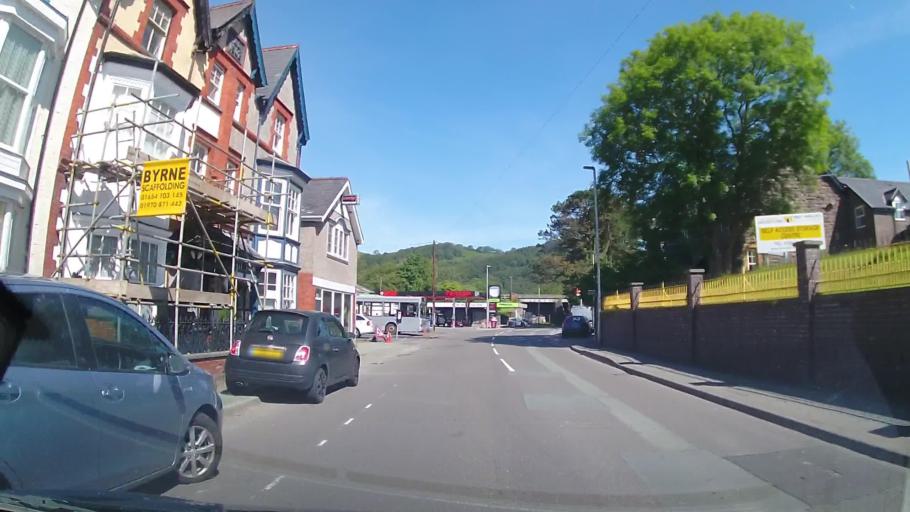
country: GB
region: Wales
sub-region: Sir Powys
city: Machynlleth
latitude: 52.5936
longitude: -3.8547
